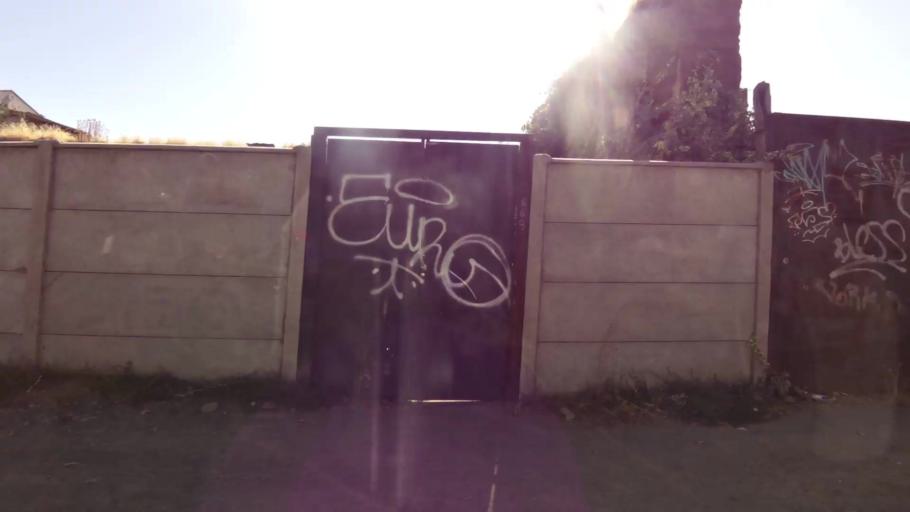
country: CL
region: Maule
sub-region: Provincia de Talca
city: Talca
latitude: -35.4318
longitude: -71.6672
